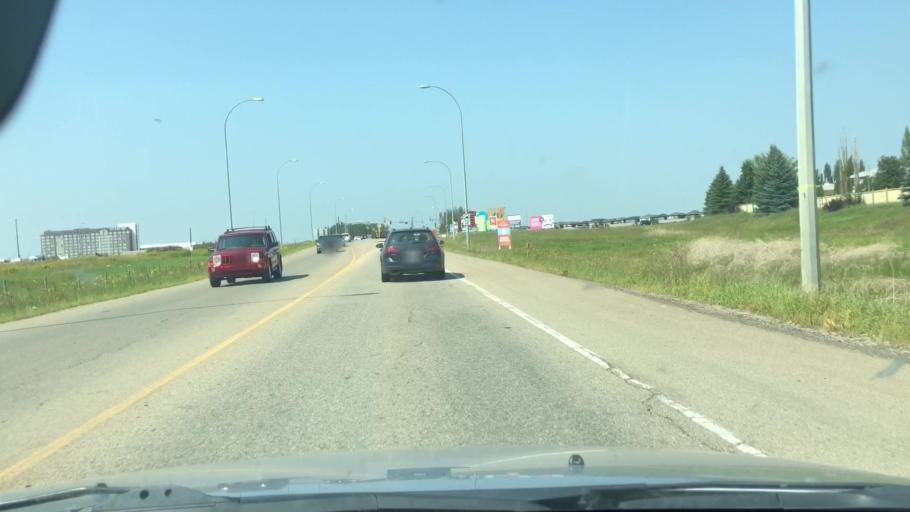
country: CA
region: Alberta
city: St. Albert
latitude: 53.5122
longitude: -113.6841
